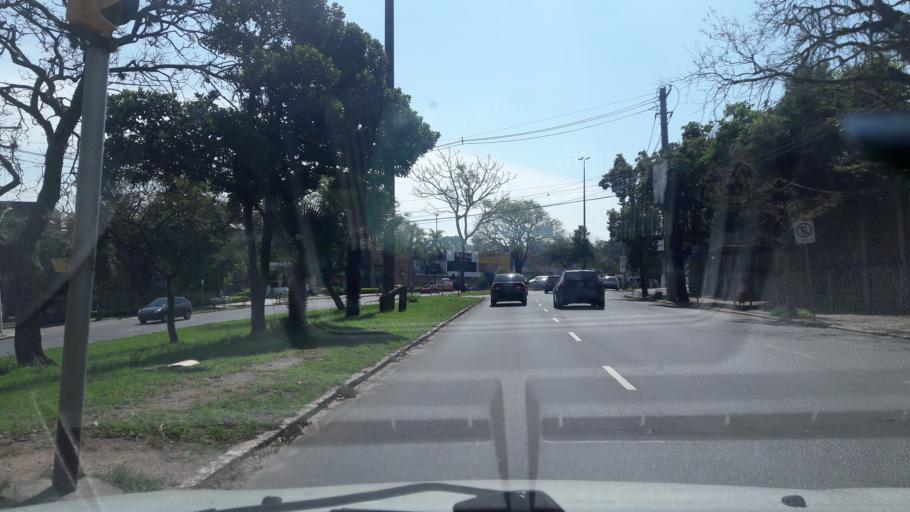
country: BR
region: Rio Grande do Sul
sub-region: Guaiba
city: Guaiba
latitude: -30.1057
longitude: -51.2537
